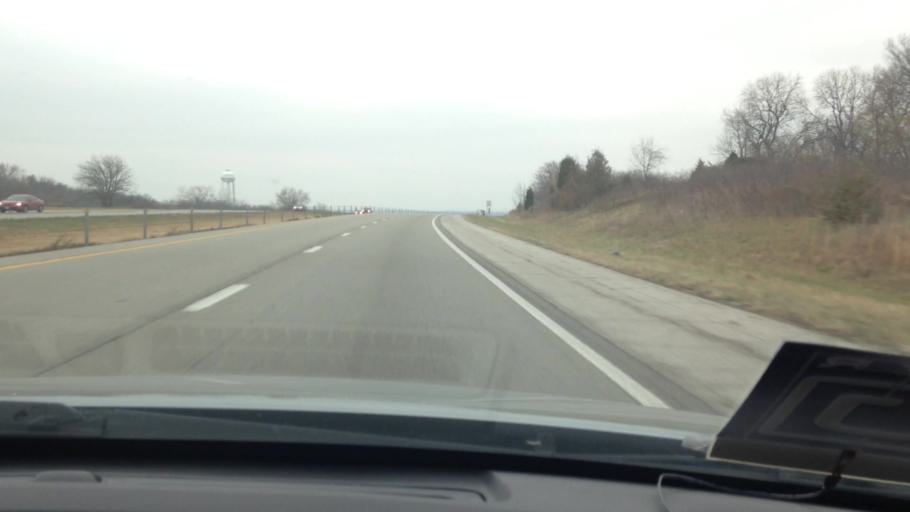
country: US
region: Missouri
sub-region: Cass County
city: Peculiar
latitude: 38.7460
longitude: -94.4762
